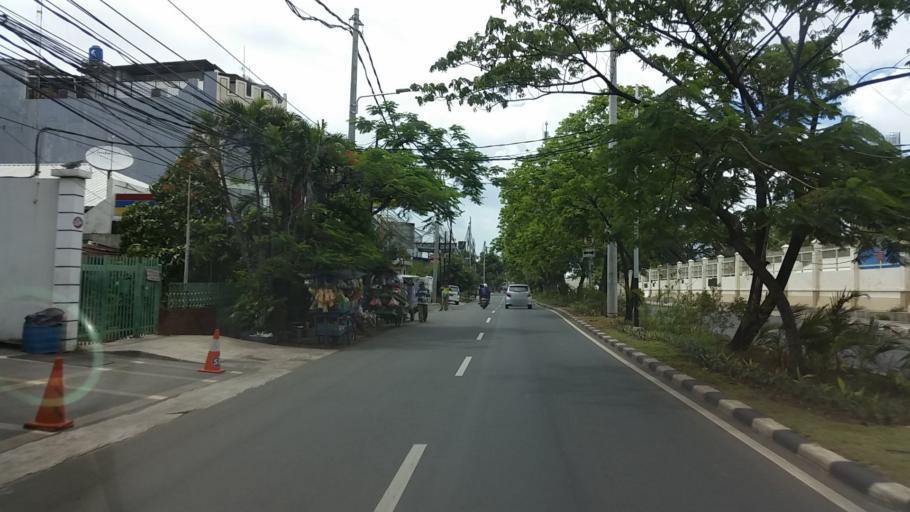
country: ID
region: Jakarta Raya
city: Jakarta
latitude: -6.1123
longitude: 106.7893
